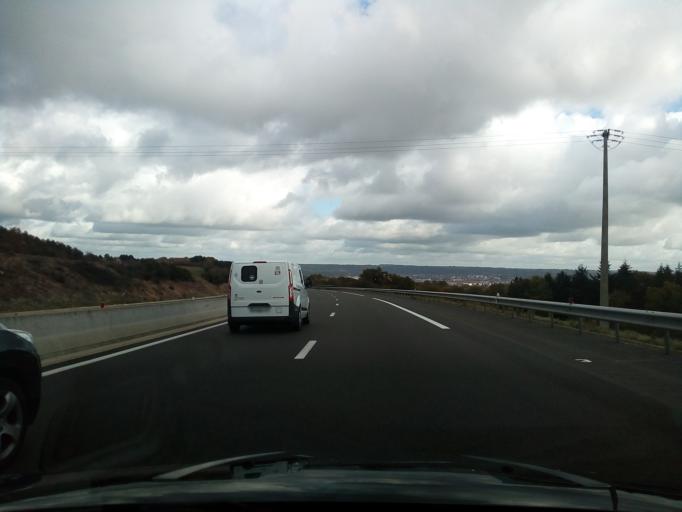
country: FR
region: Auvergne
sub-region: Departement de l'Allier
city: Premilhat
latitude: 46.3250
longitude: 2.5316
